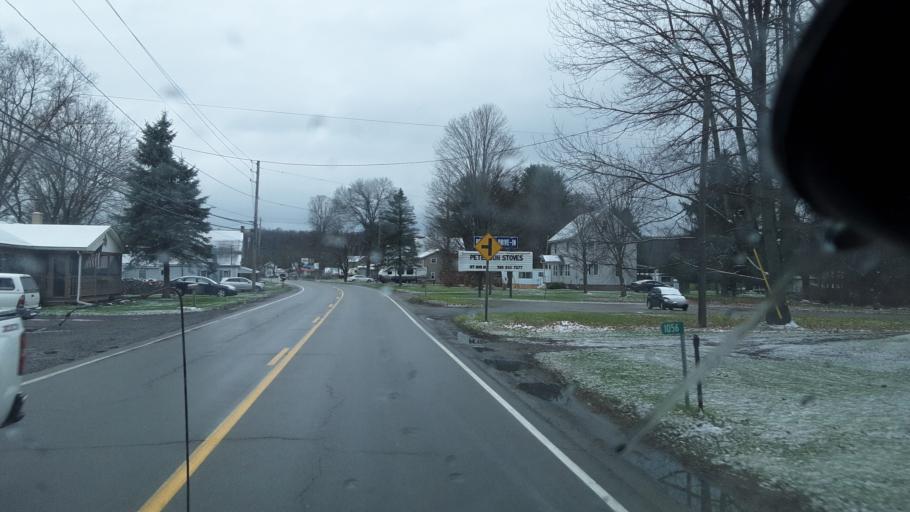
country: US
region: New York
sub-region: Cattaraugus County
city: Portville
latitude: 42.0504
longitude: -78.3542
